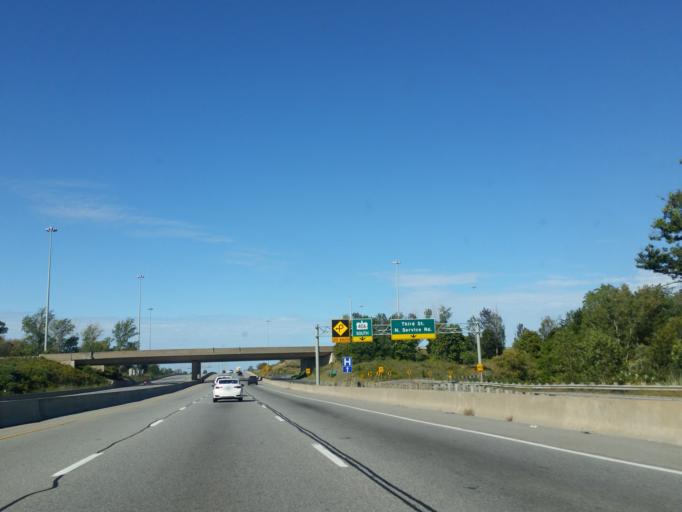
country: CA
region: Ontario
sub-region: Regional Municipality of Niagara
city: St. Catharines
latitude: 43.1774
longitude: -79.2824
